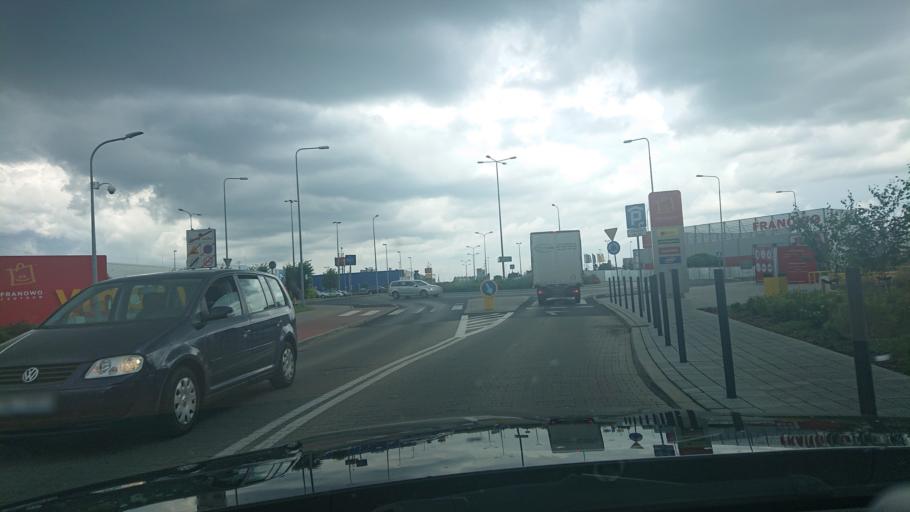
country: PL
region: Greater Poland Voivodeship
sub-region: Poznan
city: Poznan
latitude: 52.3805
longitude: 16.9836
